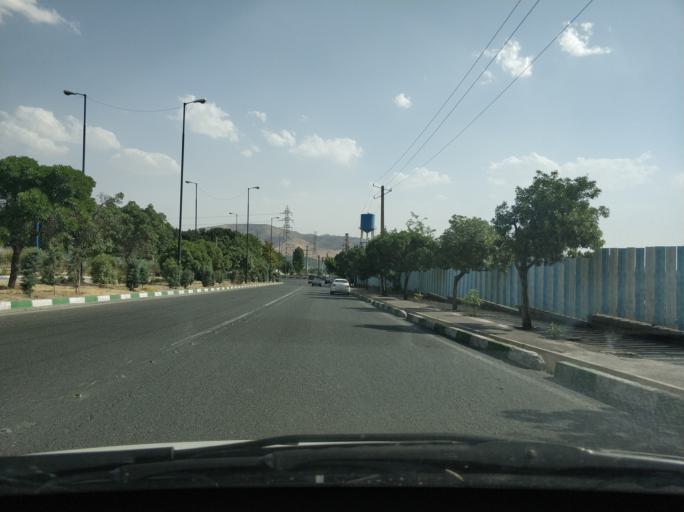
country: IR
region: Tehran
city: Tajrish
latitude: 35.7464
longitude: 51.5768
